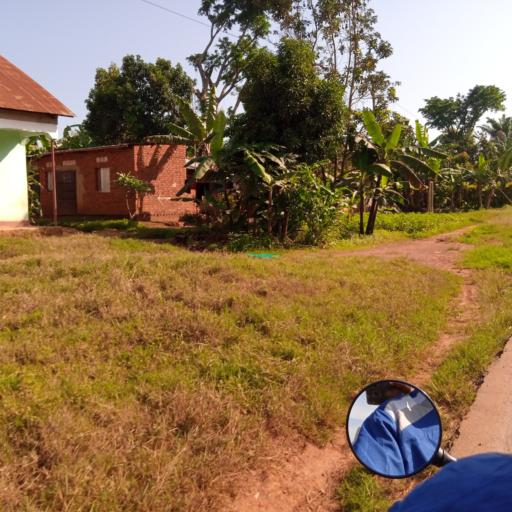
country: UG
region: Central Region
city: Masaka
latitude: -0.4526
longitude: 31.6676
